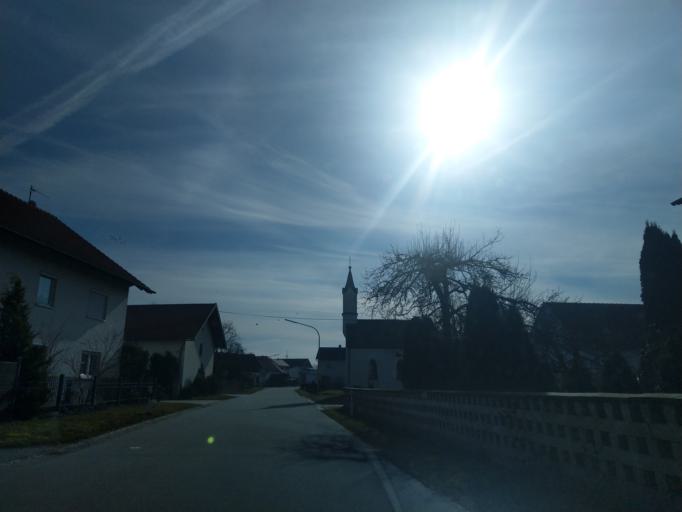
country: DE
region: Bavaria
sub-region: Lower Bavaria
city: Buchhofen
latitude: 48.6711
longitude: 12.9634
